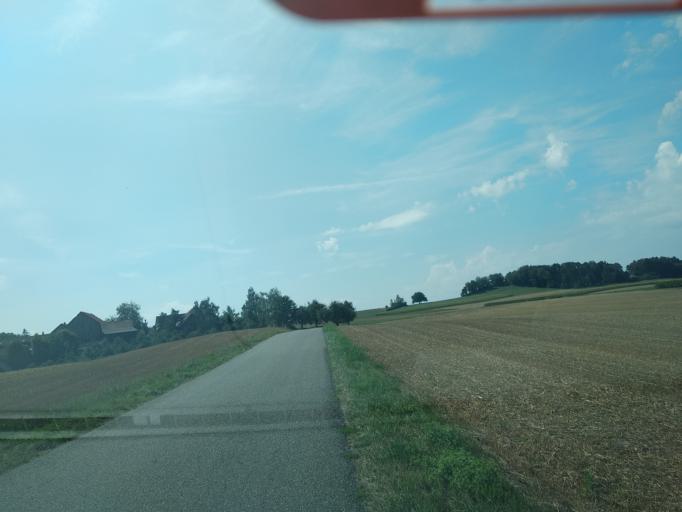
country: CH
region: Thurgau
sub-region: Frauenfeld District
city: Huttwilen
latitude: 47.5985
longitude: 8.8182
